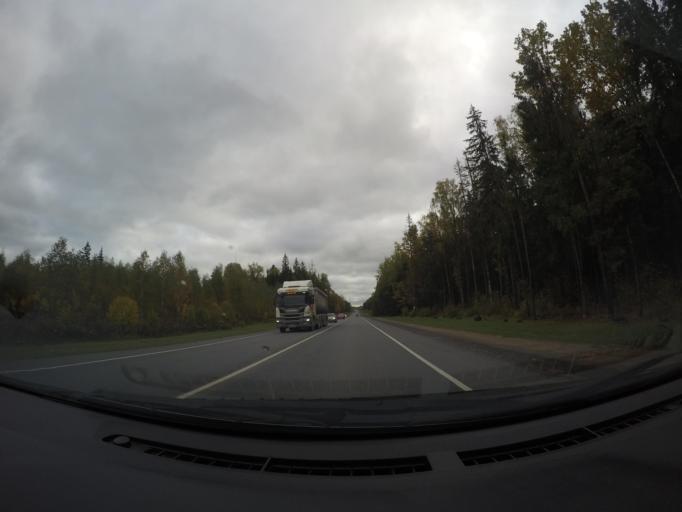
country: RU
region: Moskovskaya
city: Dorokhovo
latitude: 55.6092
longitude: 36.3527
